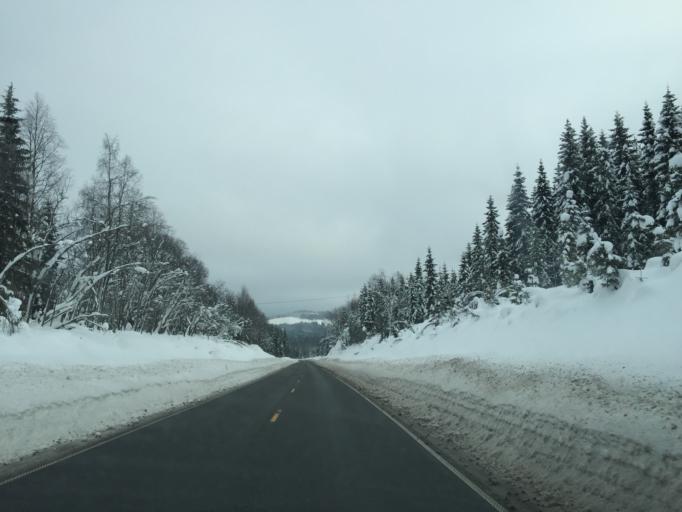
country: NO
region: Hedmark
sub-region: Trysil
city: Innbygda
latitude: 61.1184
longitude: 12.0708
